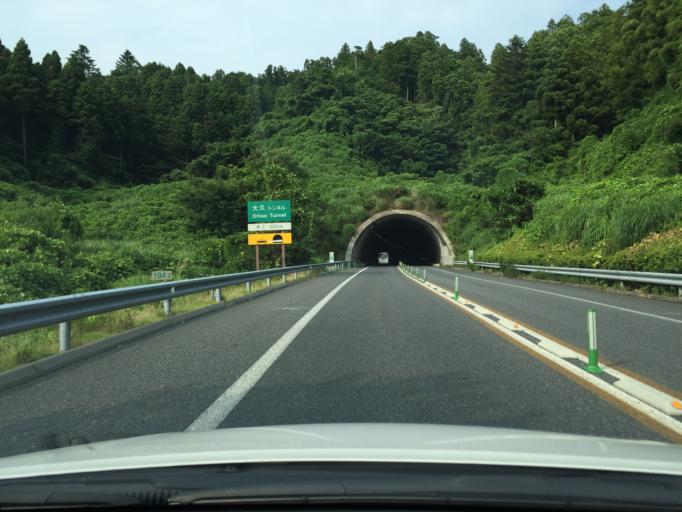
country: JP
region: Fukushima
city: Iwaki
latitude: 37.1731
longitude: 140.9712
